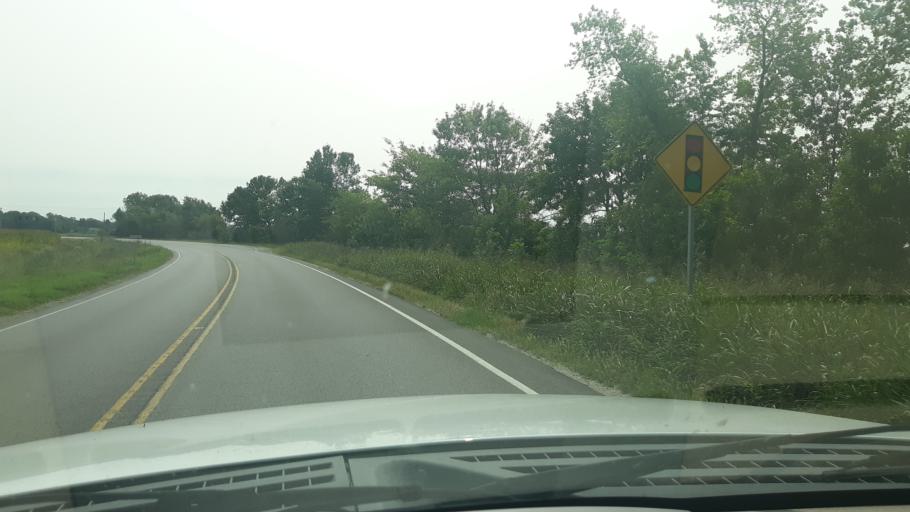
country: US
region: Indiana
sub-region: Gibson County
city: Owensville
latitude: 38.3570
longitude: -87.6910
